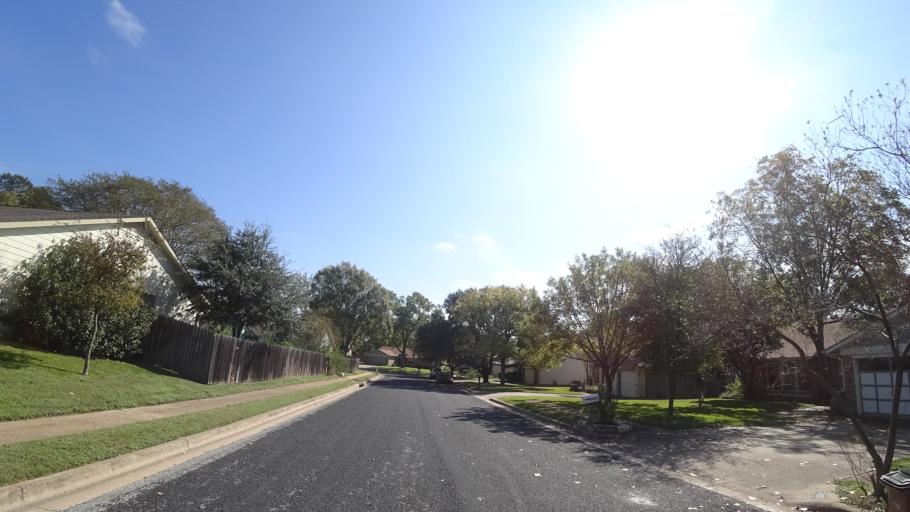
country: US
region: Texas
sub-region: Travis County
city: Shady Hollow
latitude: 30.1958
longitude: -97.8184
